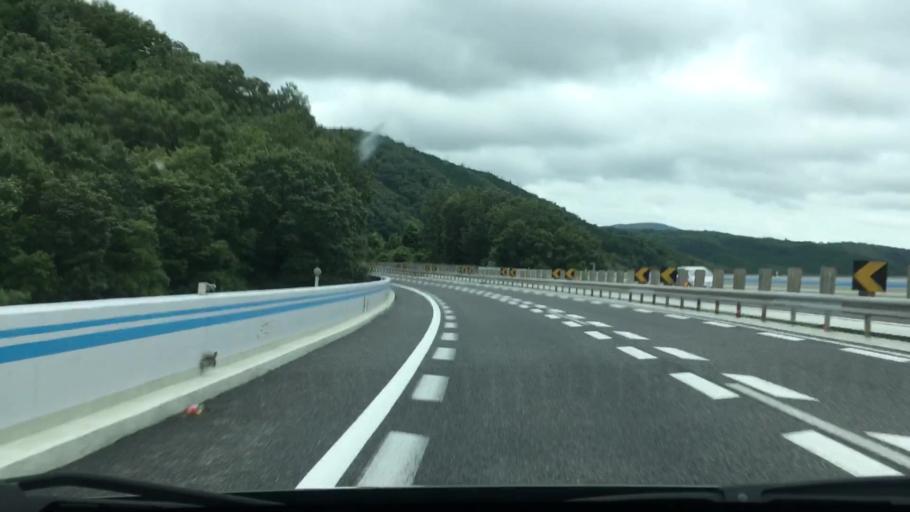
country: JP
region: Hiroshima
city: Miyoshi
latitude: 34.7838
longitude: 132.8443
